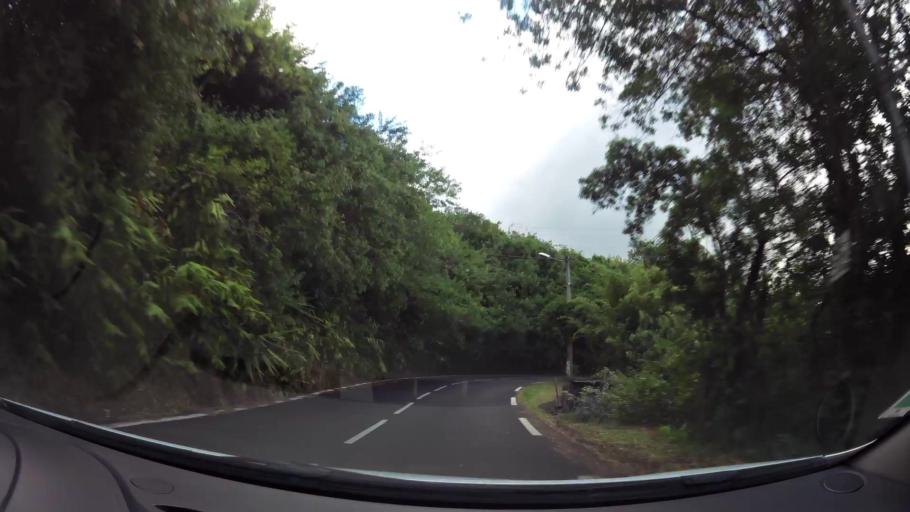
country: RE
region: Reunion
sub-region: Reunion
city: Saint-Denis
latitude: -20.9100
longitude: 55.4424
